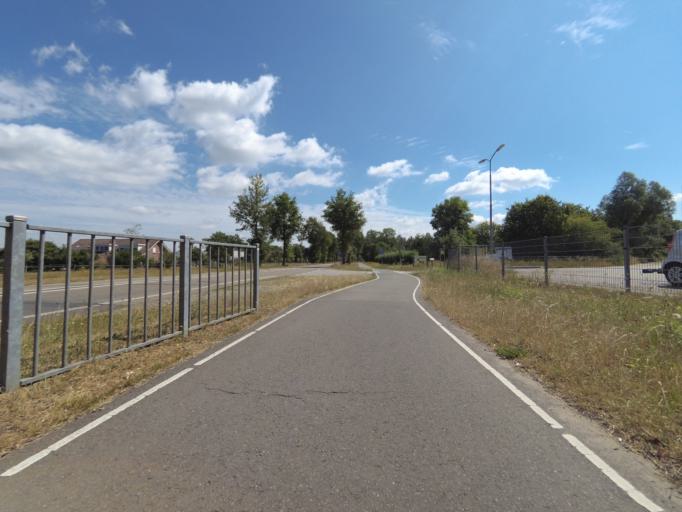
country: NL
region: Gelderland
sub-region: Gemeente Voorst
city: Voorst
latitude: 52.1781
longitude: 6.0844
